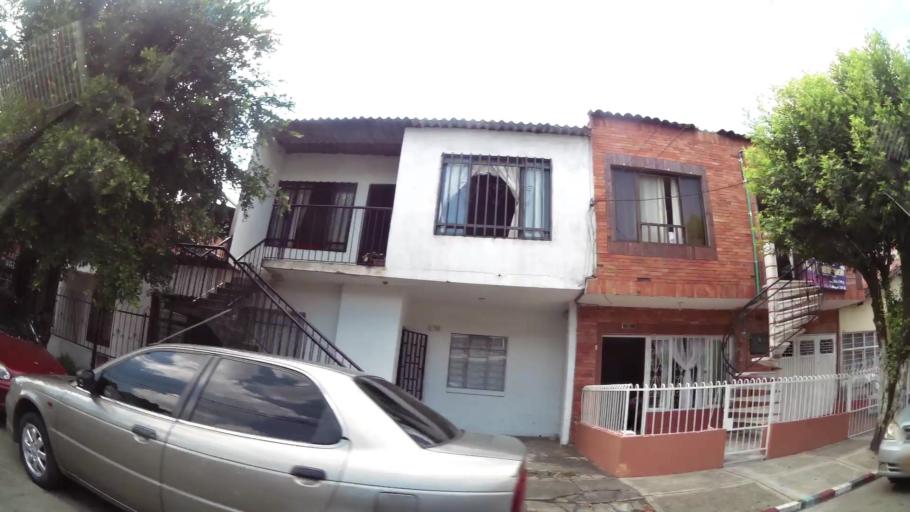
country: CO
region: Valle del Cauca
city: Cali
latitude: 3.4135
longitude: -76.5154
